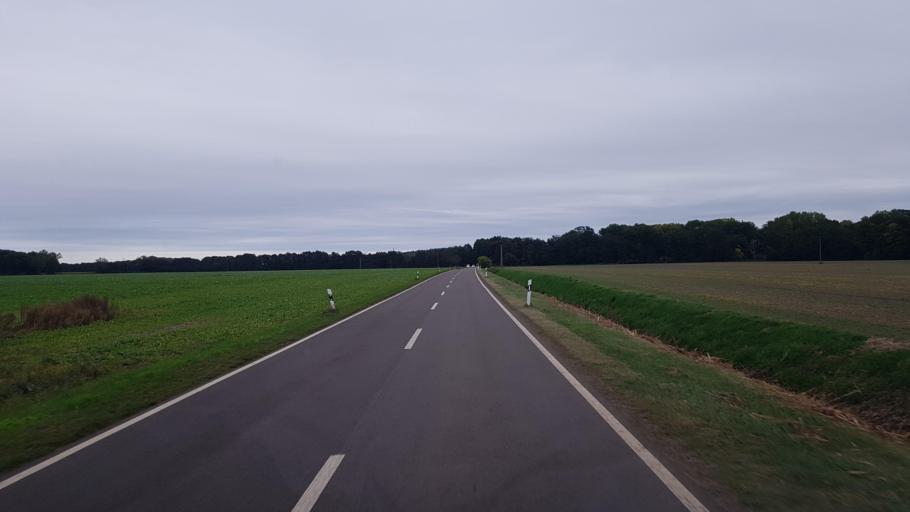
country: DE
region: Brandenburg
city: Drahnsdorf
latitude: 51.8956
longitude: 13.6338
